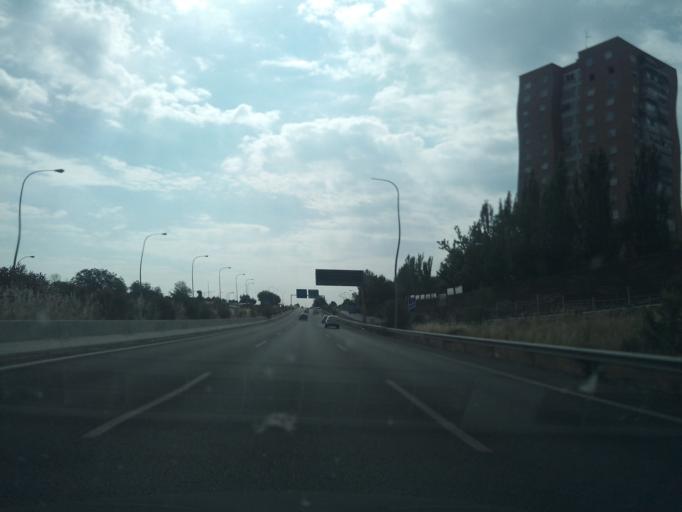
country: ES
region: Madrid
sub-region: Provincia de Madrid
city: Hortaleza
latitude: 40.4810
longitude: -3.6492
